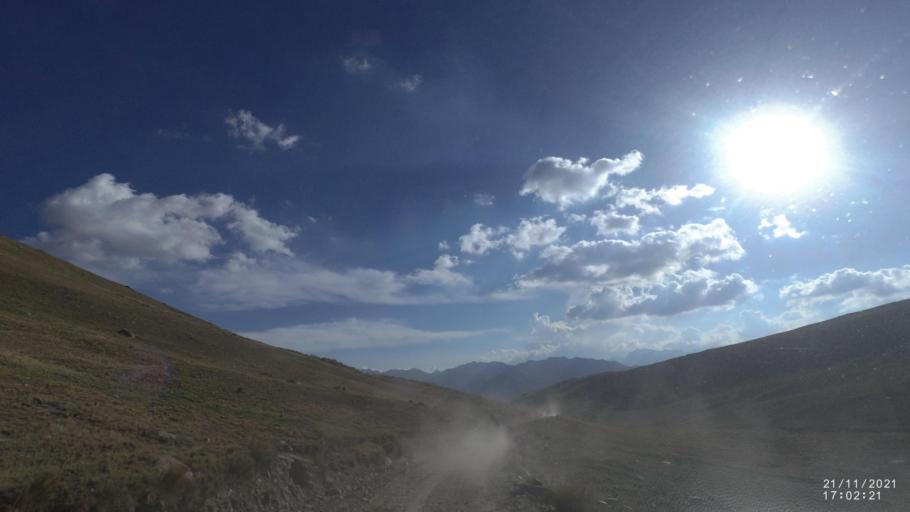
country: BO
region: Cochabamba
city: Cochabamba
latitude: -17.1162
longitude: -66.2543
